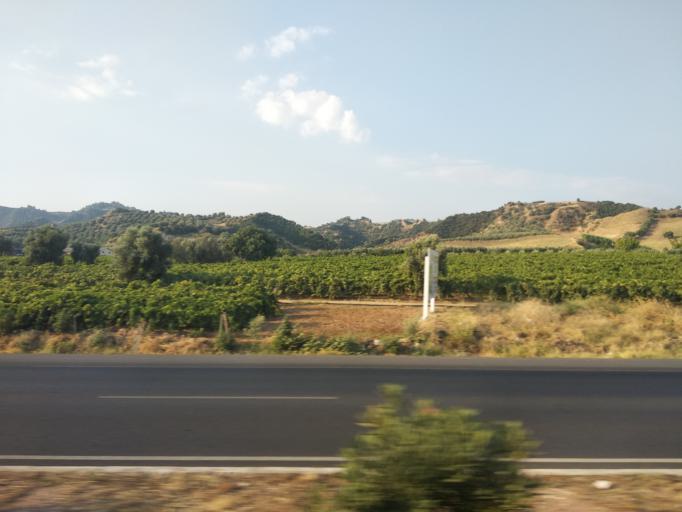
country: TR
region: Manisa
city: Ahmetli
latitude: 38.5085
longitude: 27.9849
